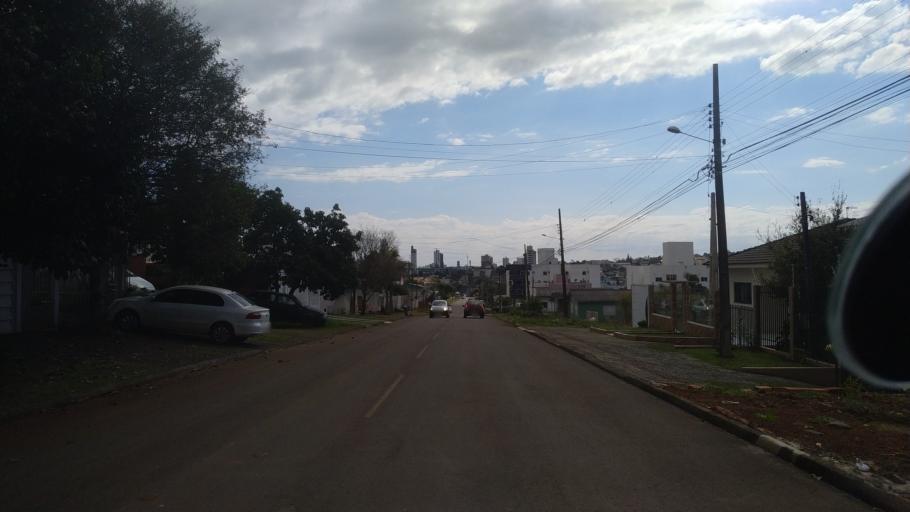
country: BR
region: Santa Catarina
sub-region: Chapeco
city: Chapeco
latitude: -27.1161
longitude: -52.6031
